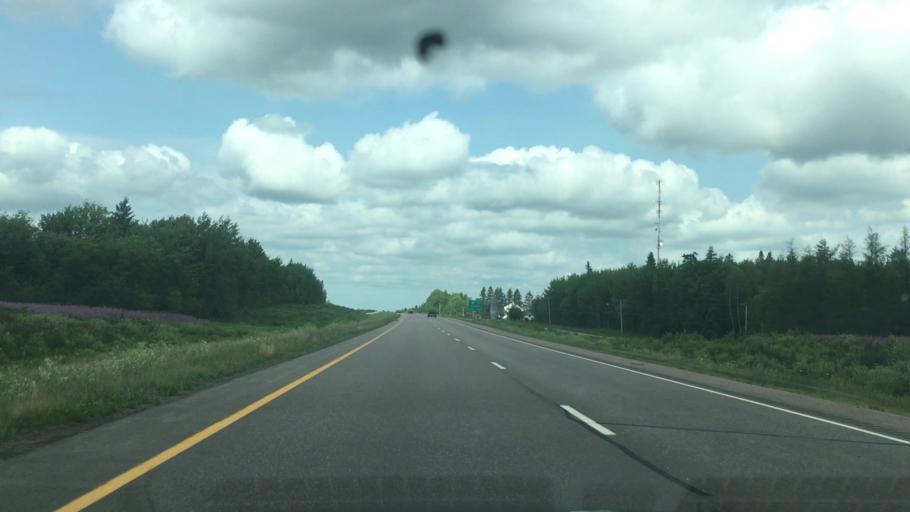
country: CA
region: New Brunswick
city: Dieppe
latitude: 46.0815
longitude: -64.5936
